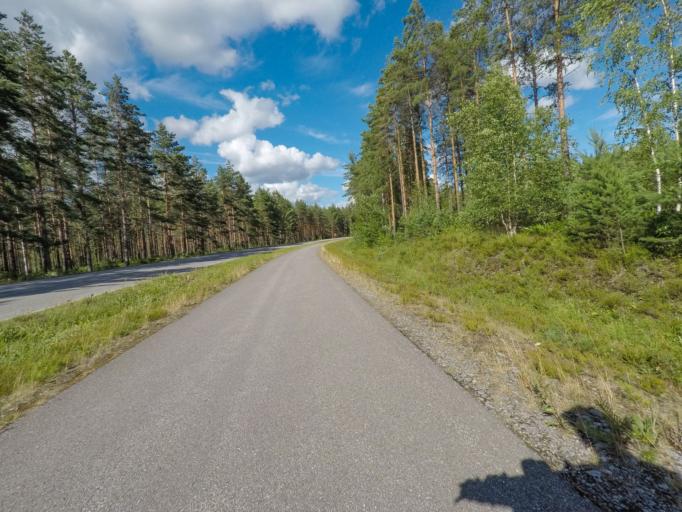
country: FI
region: South Karelia
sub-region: Lappeenranta
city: Joutseno
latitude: 61.1484
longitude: 28.5516
